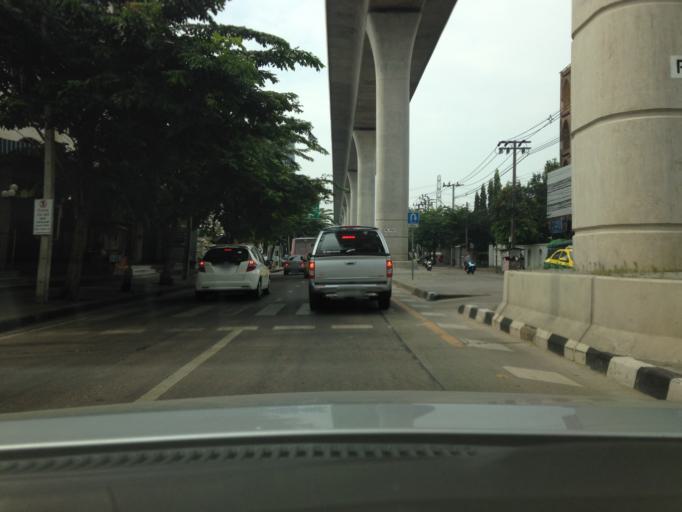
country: TH
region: Bangkok
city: Bang Sue
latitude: 13.8258
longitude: 100.5313
